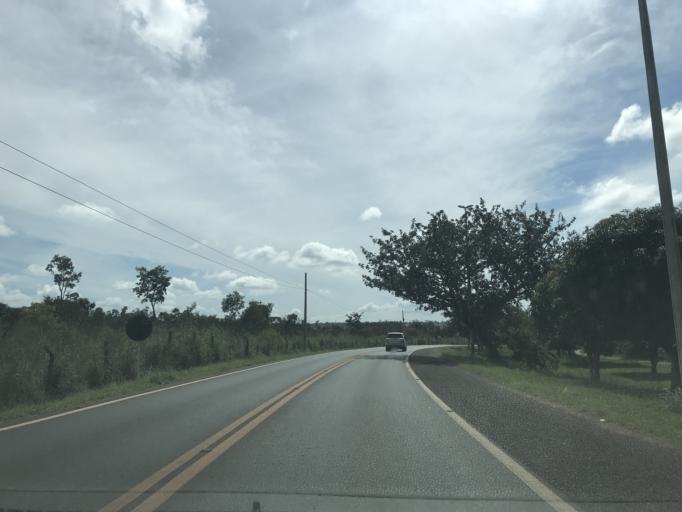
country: BR
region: Federal District
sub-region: Brasilia
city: Brasilia
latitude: -15.6881
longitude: -47.8366
